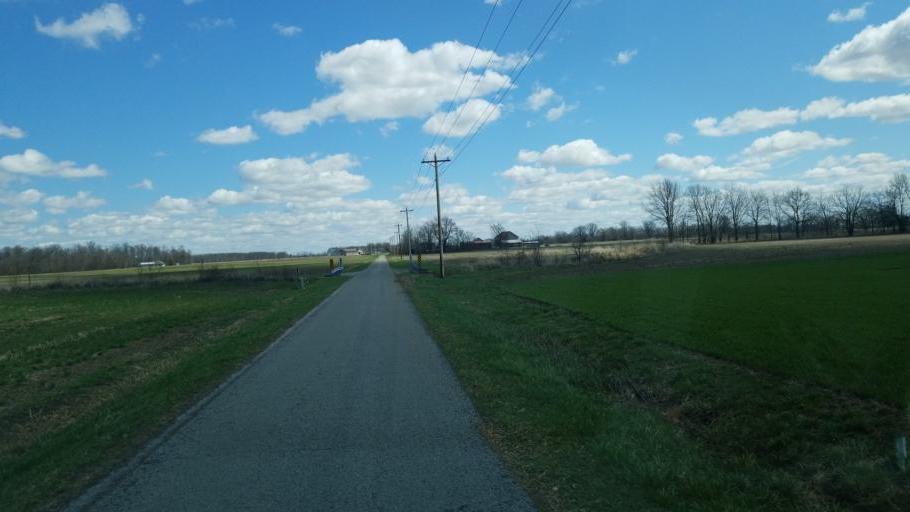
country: US
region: Ohio
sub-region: Hancock County
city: Arlington
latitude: 40.9538
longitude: -83.5314
